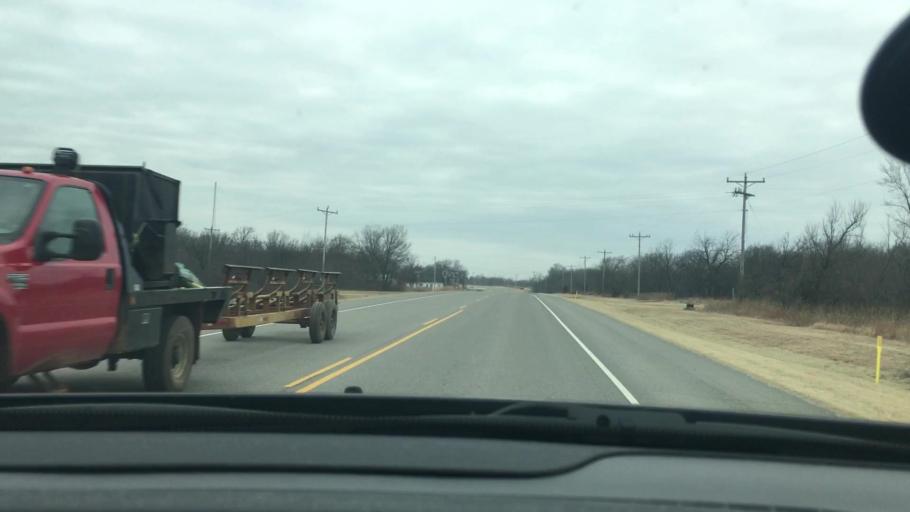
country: US
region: Oklahoma
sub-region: Carter County
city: Healdton
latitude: 34.4792
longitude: -97.4653
